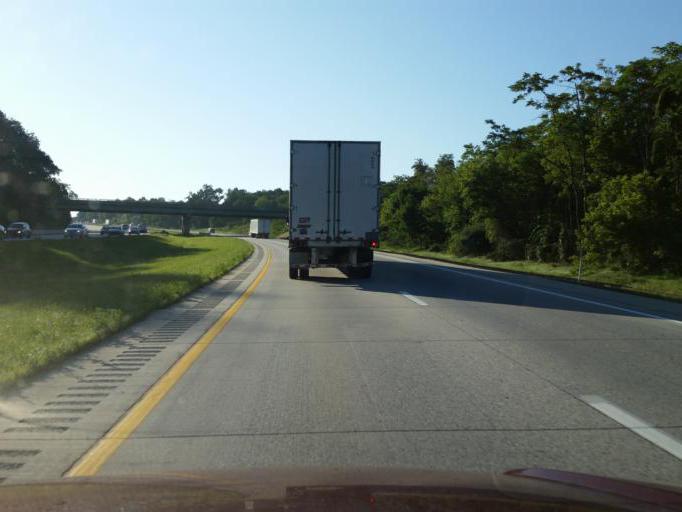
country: US
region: Pennsylvania
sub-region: Dauphin County
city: Middletown
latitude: 40.1948
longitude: -76.6878
